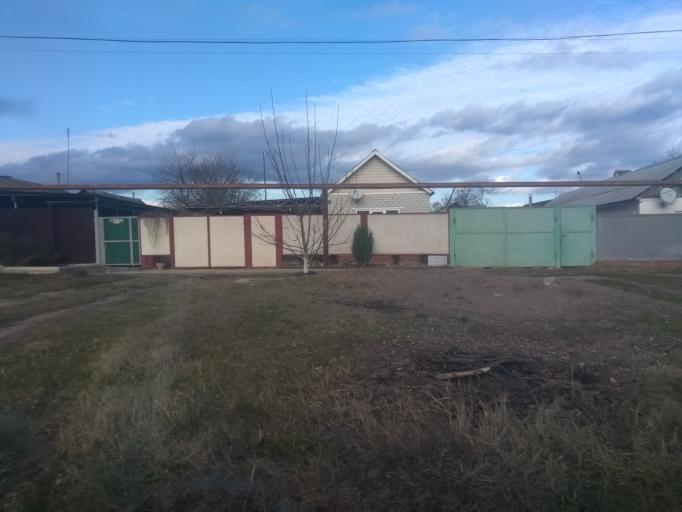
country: RU
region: Stavropol'skiy
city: Krasnokumskoye
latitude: 44.1760
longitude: 43.4834
